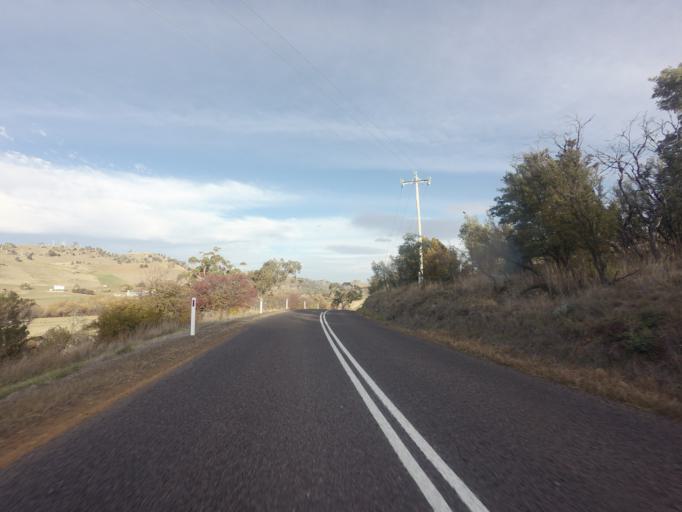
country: AU
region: Tasmania
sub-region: Brighton
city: Bridgewater
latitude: -42.4278
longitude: 147.1418
